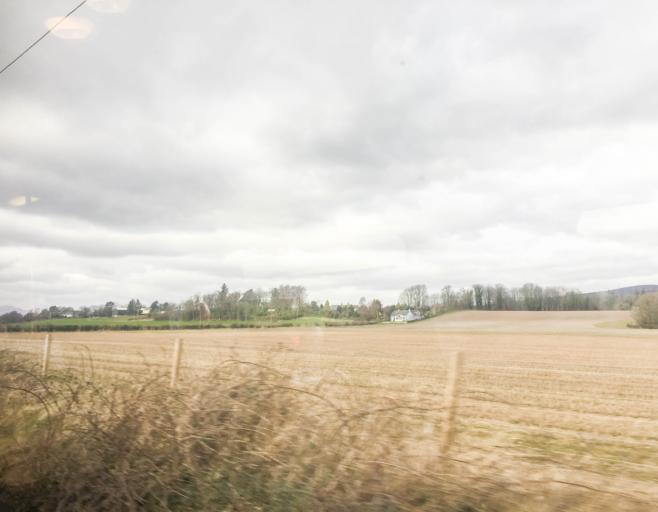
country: GB
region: Scotland
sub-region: Argyll and Bute
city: Cardross
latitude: 55.9618
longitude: -4.6612
